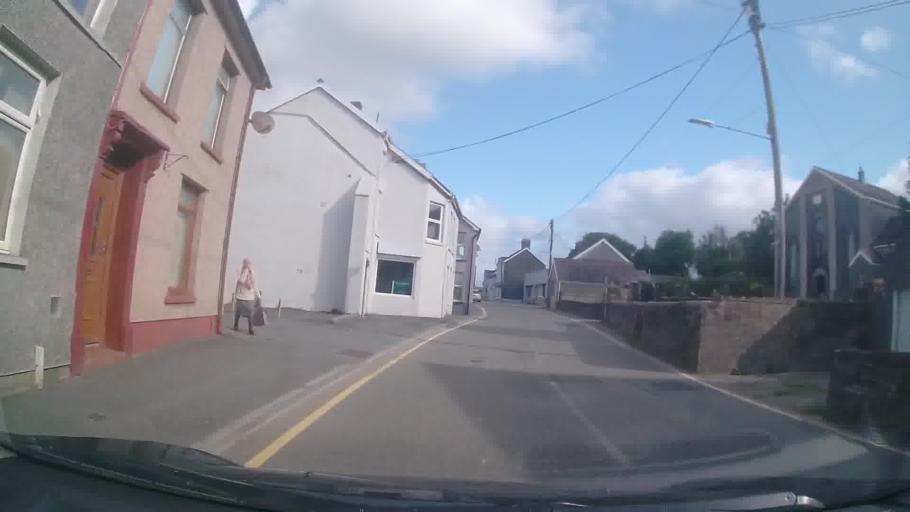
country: GB
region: Wales
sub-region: Carmarthenshire
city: Saint Clears
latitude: 51.8209
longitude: -4.4937
